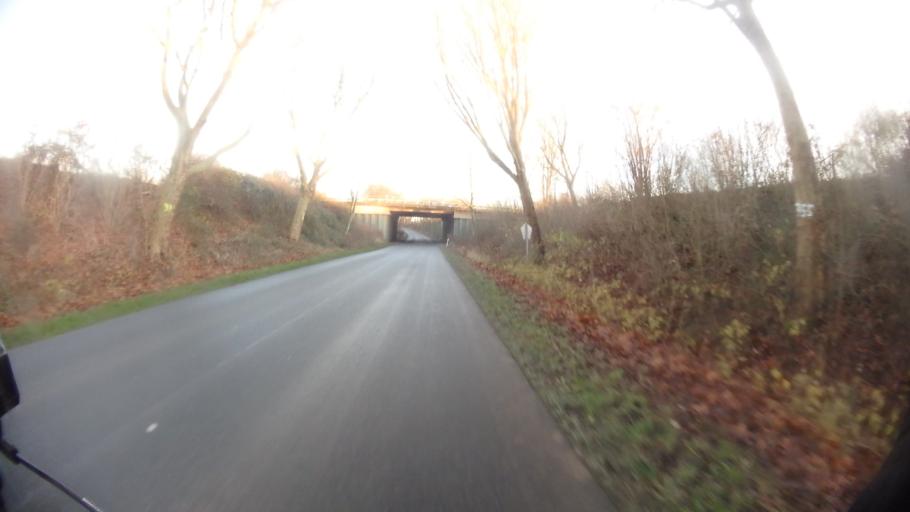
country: DE
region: Schleswig-Holstein
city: Scharbeutz
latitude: 54.0189
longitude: 10.7294
